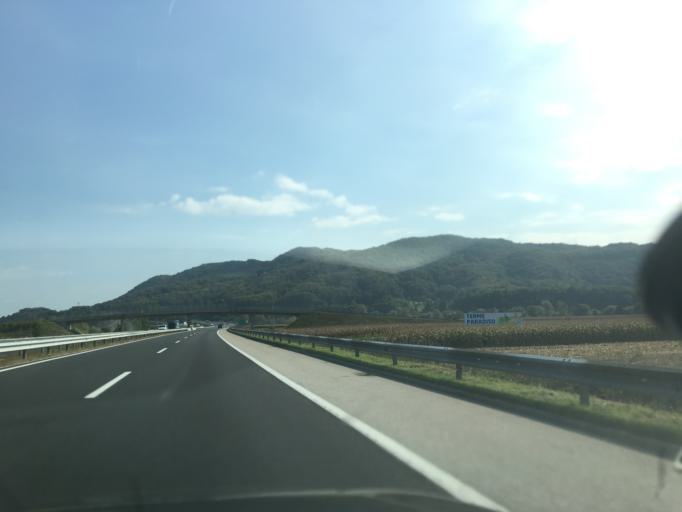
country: SI
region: Brezice
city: Brezice
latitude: 45.8996
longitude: 15.5756
